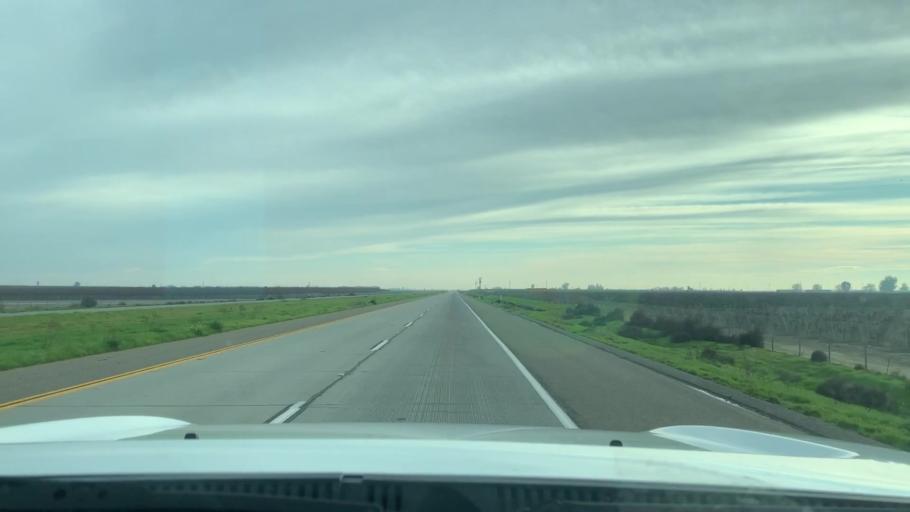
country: US
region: California
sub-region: Fresno County
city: Easton
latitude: 36.5897
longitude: -119.7862
